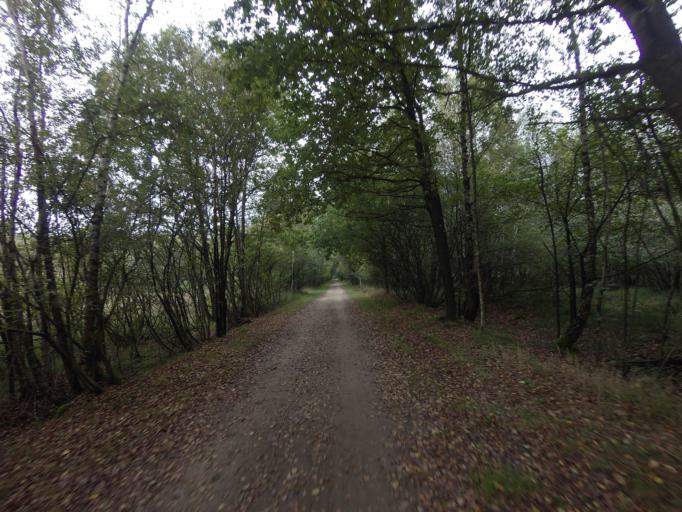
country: DE
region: North Rhine-Westphalia
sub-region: Regierungsbezirk Munster
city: Gronau
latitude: 52.2479
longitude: 7.0909
